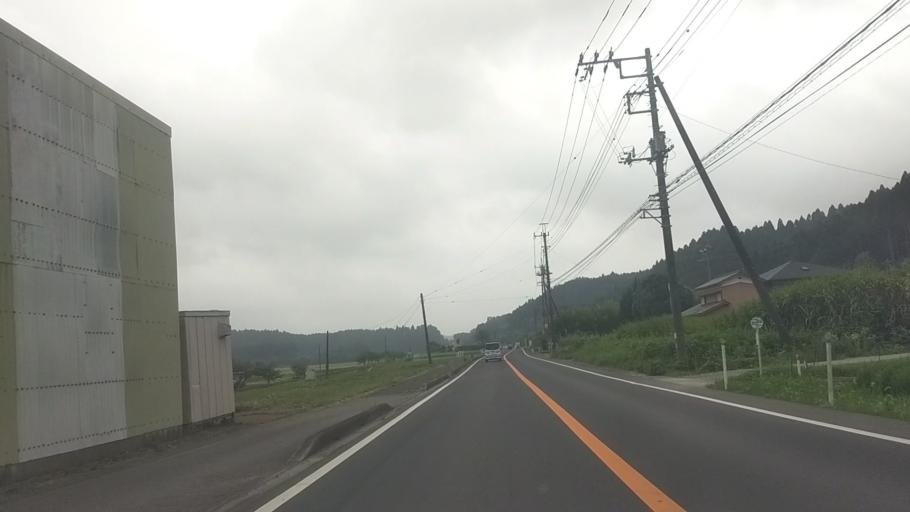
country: JP
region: Chiba
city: Ohara
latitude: 35.2764
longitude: 140.3279
